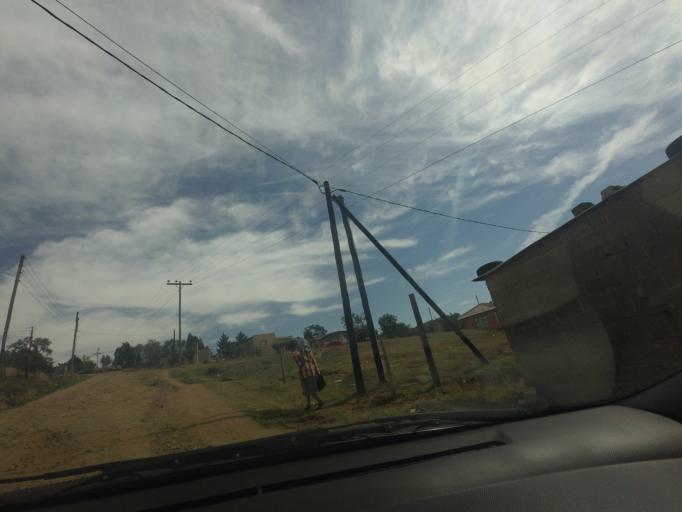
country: LS
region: Berea
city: Teyateyaneng
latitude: -29.1512
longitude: 27.7550
